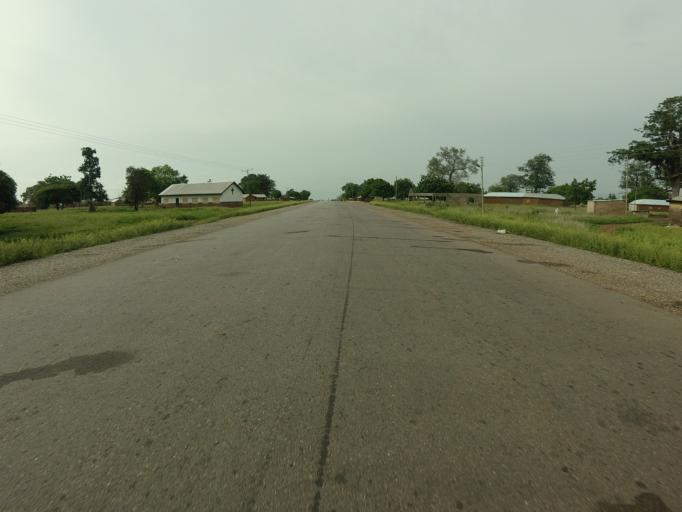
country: GH
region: Northern
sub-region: Yendi
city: Yendi
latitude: 9.6406
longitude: -0.0652
